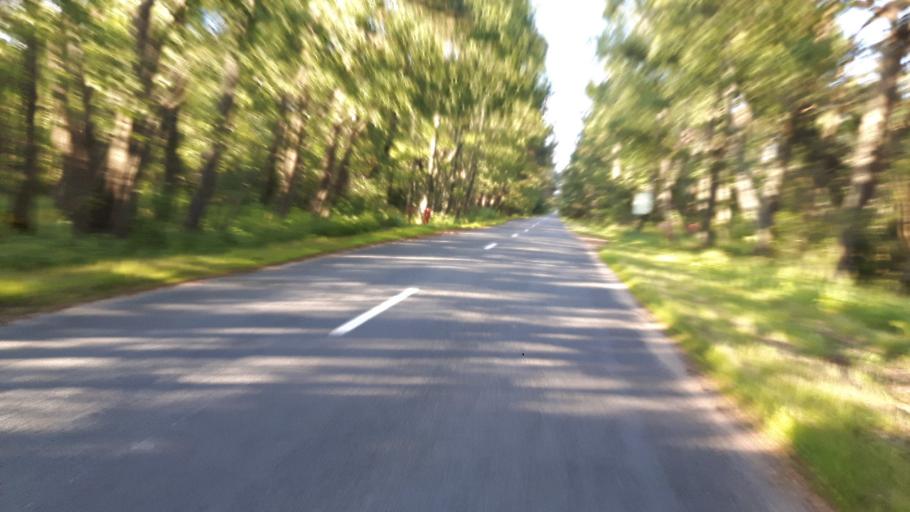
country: LT
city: Nida
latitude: 55.2517
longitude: 20.9282
